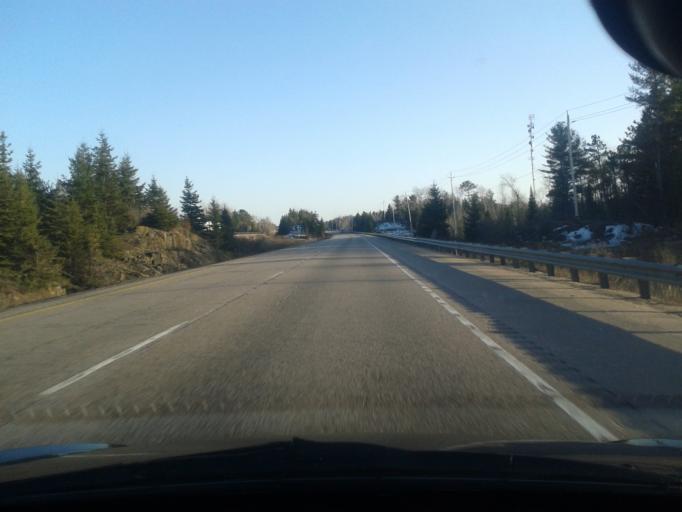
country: CA
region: Ontario
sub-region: Nipissing District
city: North Bay
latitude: 46.2302
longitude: -79.3496
